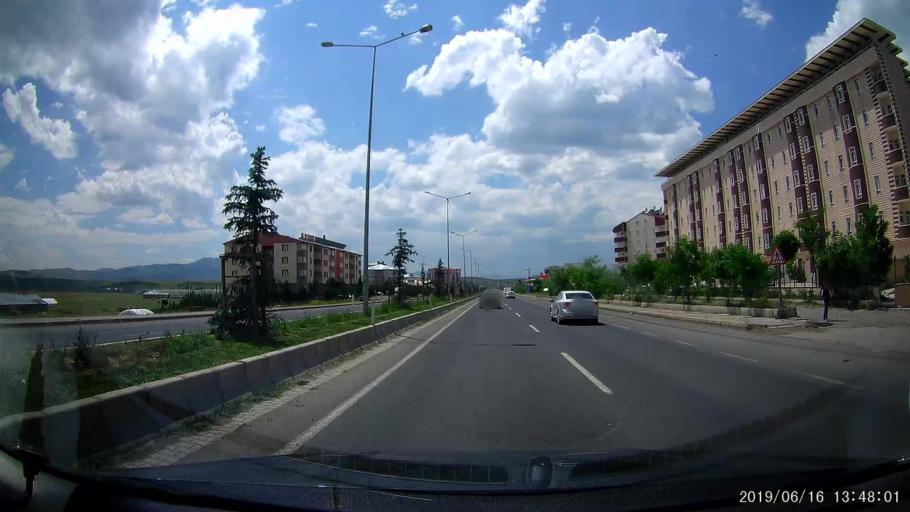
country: TR
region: Agri
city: Agri
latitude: 39.7143
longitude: 43.0149
